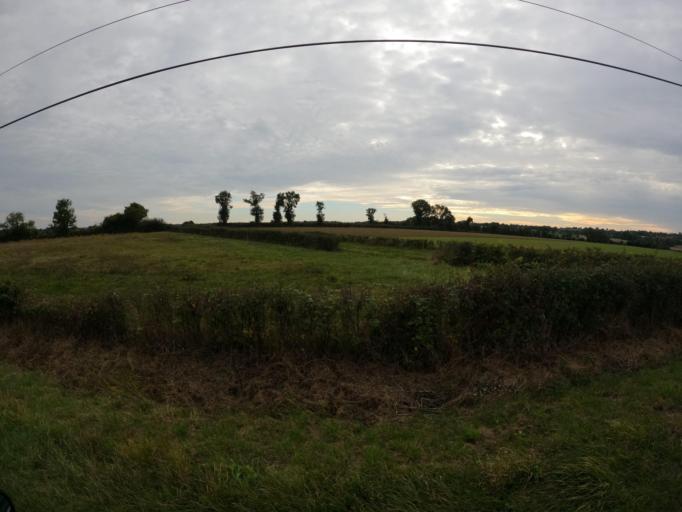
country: FR
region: Pays de la Loire
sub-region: Departement de Maine-et-Loire
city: Saint-Christophe-du-Bois
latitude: 47.0269
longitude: -0.9582
